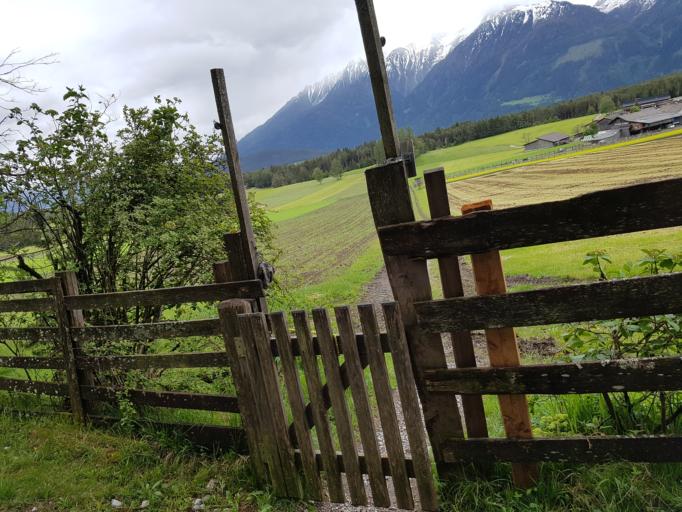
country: AT
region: Tyrol
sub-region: Politischer Bezirk Imst
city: Obsteig
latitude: 47.3121
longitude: 10.9421
